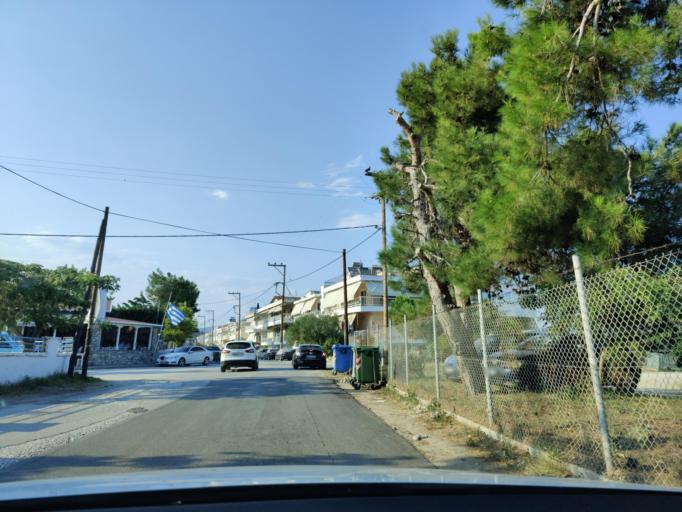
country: GR
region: East Macedonia and Thrace
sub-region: Nomos Kavalas
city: Nea Peramos
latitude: 40.8304
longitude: 24.3048
